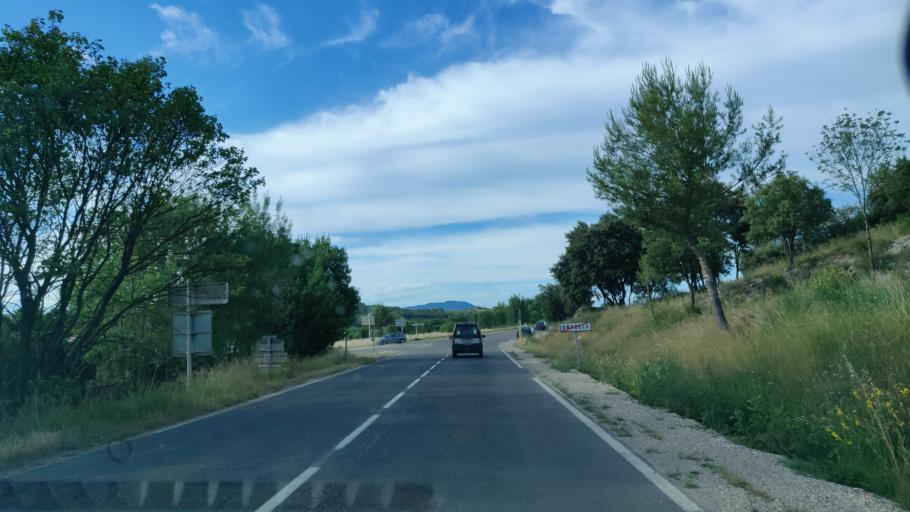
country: FR
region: Languedoc-Roussillon
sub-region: Departement de l'Herault
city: Grabels
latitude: 43.6595
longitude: 3.7931
